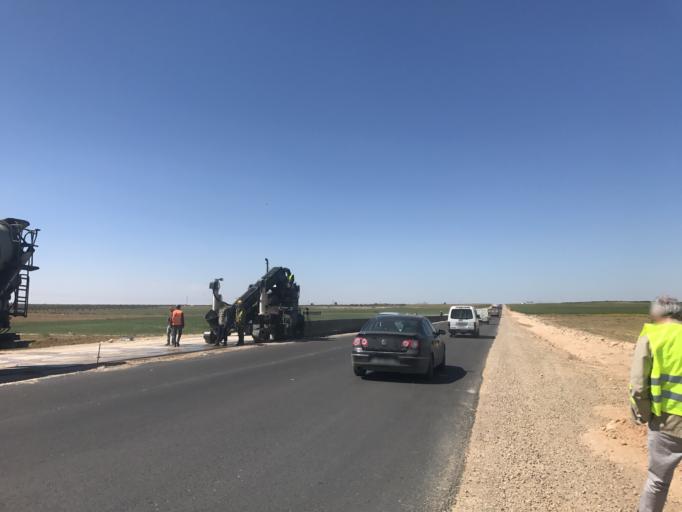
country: TN
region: Susah
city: Sidi el Hani
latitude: 35.6895
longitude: 10.3653
